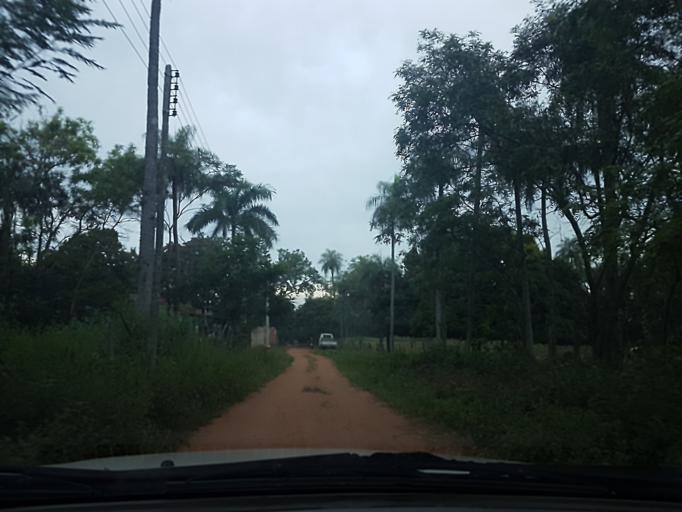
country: PY
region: Central
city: Limpio
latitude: -25.2417
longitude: -57.4609
